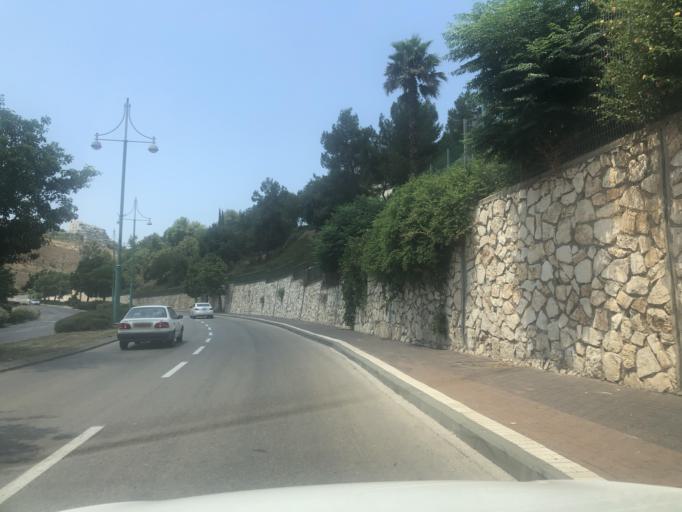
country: IL
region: Haifa
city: Daliyat el Karmil
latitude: 32.6522
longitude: 35.1045
